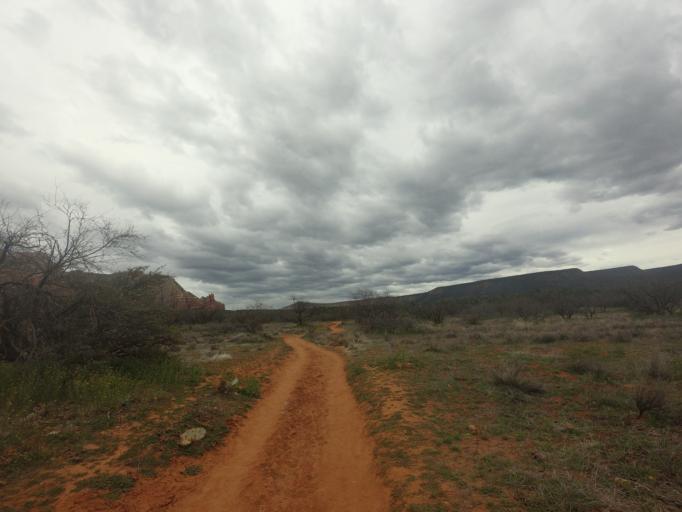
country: US
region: Arizona
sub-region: Yavapai County
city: Village of Oak Creek (Big Park)
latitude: 34.7973
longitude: -111.7528
